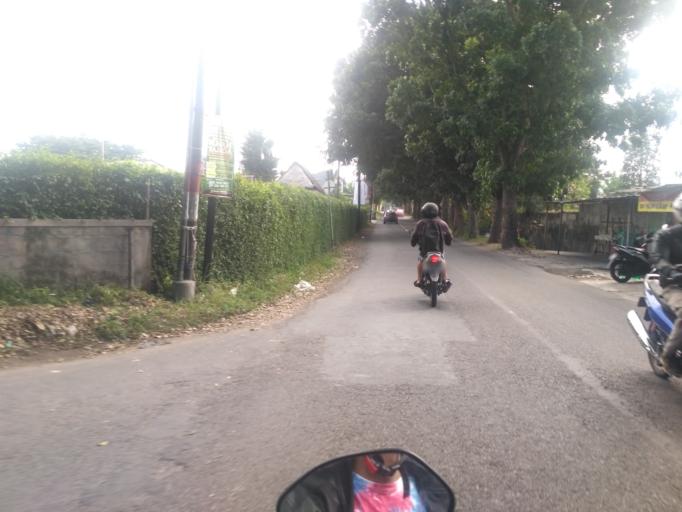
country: ID
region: Daerah Istimewa Yogyakarta
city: Yogyakarta
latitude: -7.7615
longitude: 110.3454
